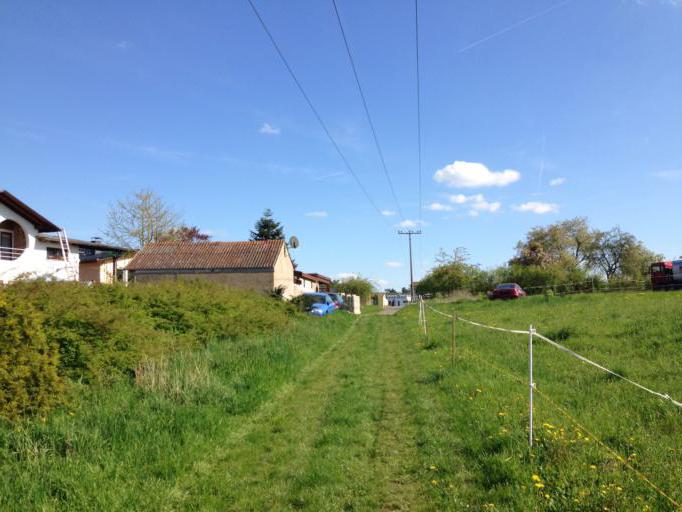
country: DE
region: Hesse
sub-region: Regierungsbezirk Giessen
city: Grunberg
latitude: 50.5612
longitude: 8.8968
